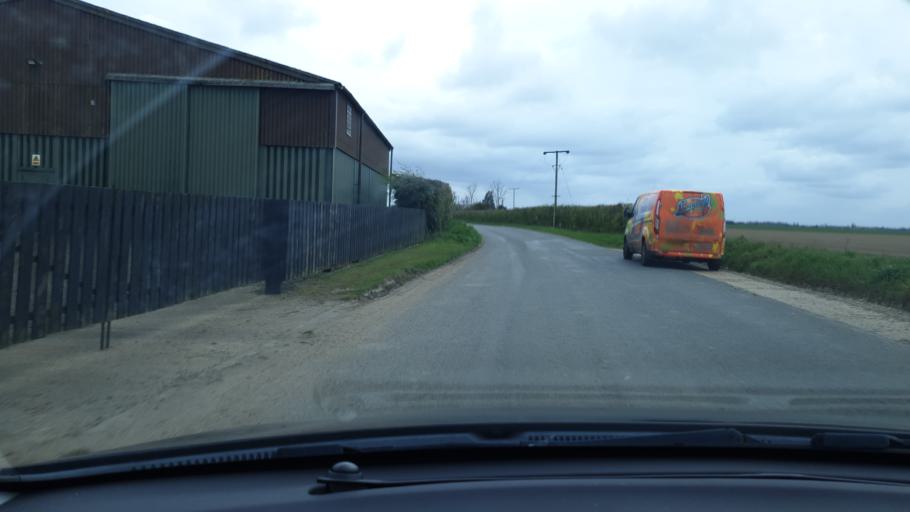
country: GB
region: England
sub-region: Essex
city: Mistley
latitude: 51.9249
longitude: 1.1773
